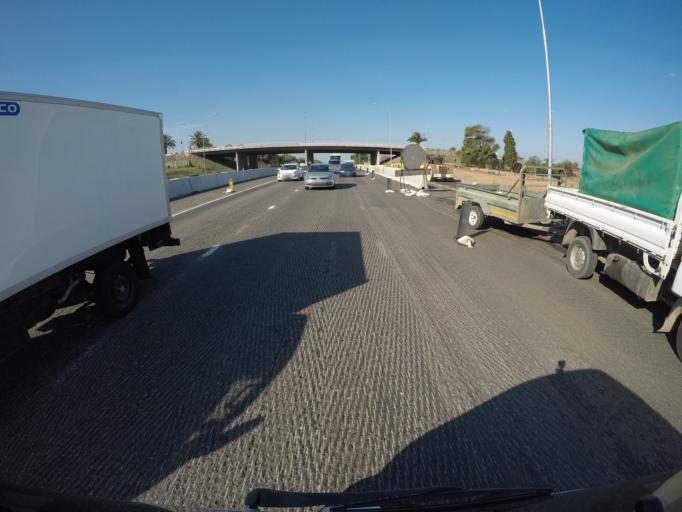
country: ZA
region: Western Cape
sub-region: City of Cape Town
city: Kraaifontein
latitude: -33.8828
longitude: 18.6454
